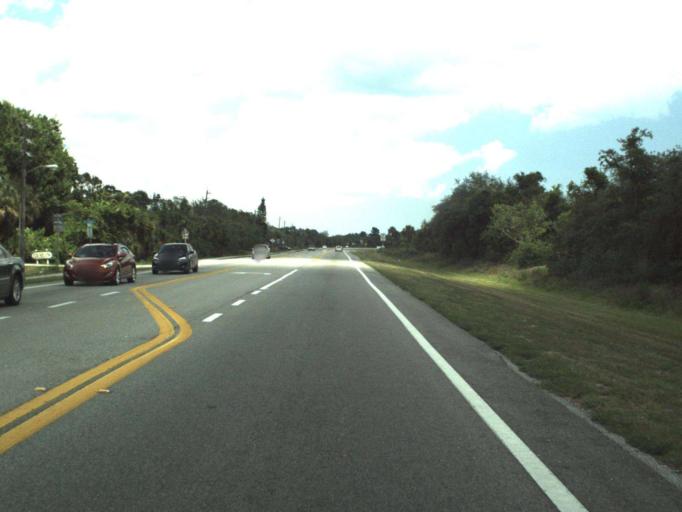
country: US
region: Florida
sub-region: Brevard County
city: Titusville
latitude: 28.5860
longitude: -80.8470
